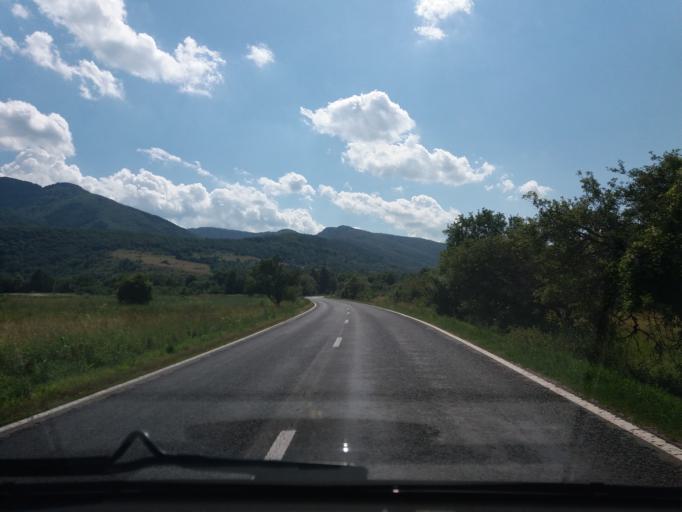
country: RO
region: Hunedoara
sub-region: Comuna Sarmizegetusa
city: Sarmizegetusa
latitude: 45.5074
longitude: 22.7301
